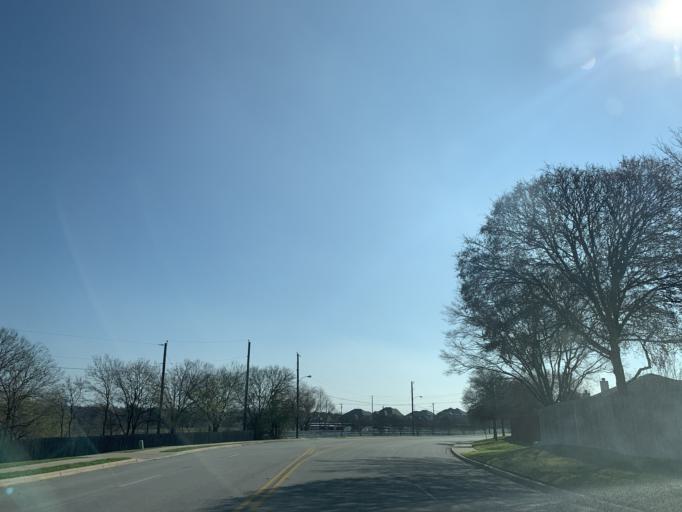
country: US
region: Texas
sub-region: Travis County
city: Windemere
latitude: 30.4984
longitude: -97.6369
